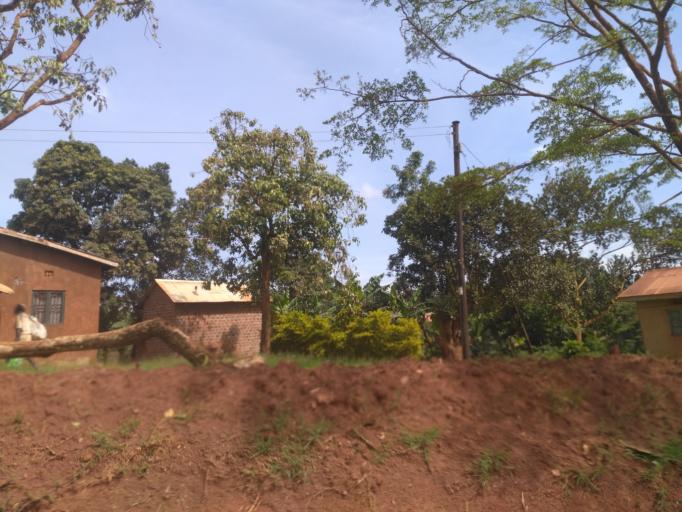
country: UG
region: Central Region
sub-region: Wakiso District
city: Kireka
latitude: 0.4412
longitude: 32.5892
